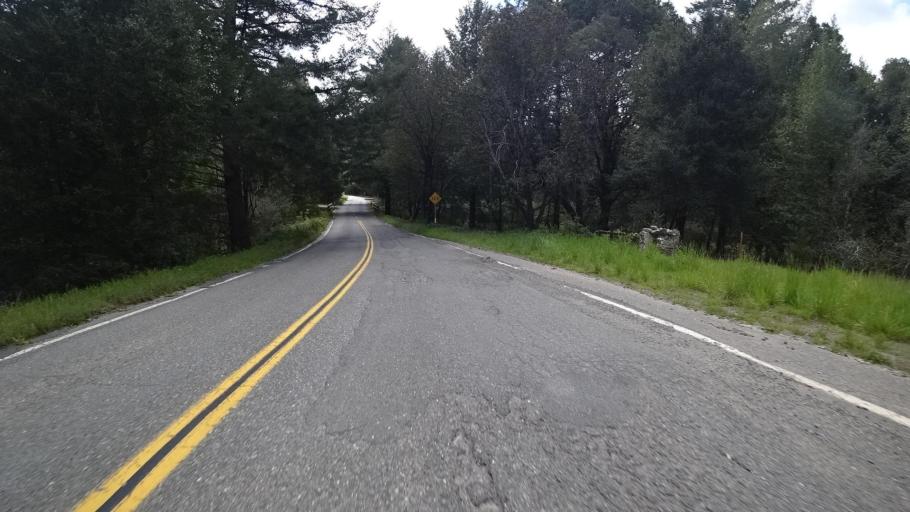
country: US
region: California
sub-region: Humboldt County
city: Redway
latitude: 40.0630
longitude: -123.9635
